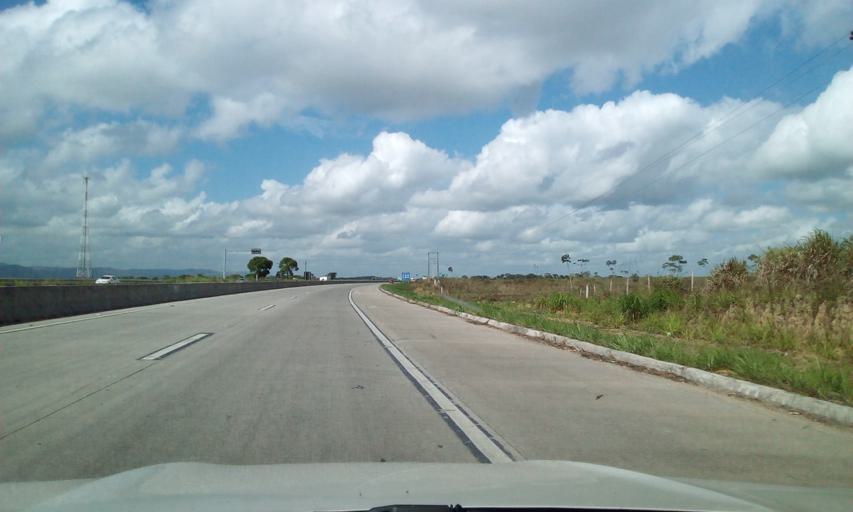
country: BR
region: Alagoas
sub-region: Messias
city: Messias
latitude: -9.3899
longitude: -35.8350
